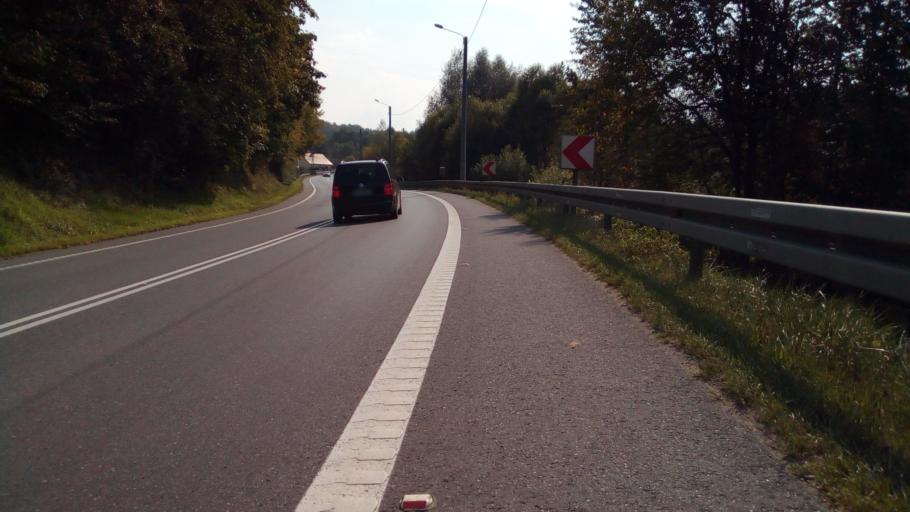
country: PL
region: Subcarpathian Voivodeship
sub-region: Powiat strzyzowski
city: Jawornik
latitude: 49.8504
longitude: 21.8966
